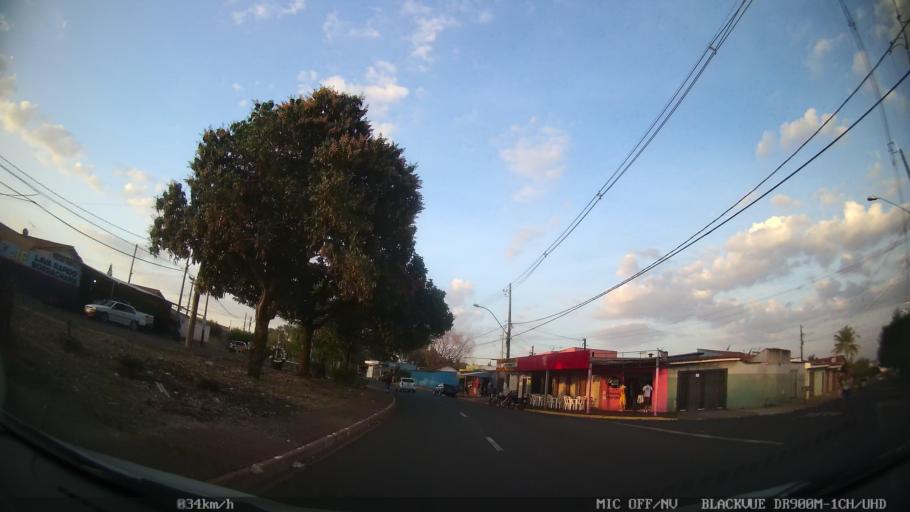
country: BR
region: Sao Paulo
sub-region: Ribeirao Preto
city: Ribeirao Preto
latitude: -21.1257
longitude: -47.8264
